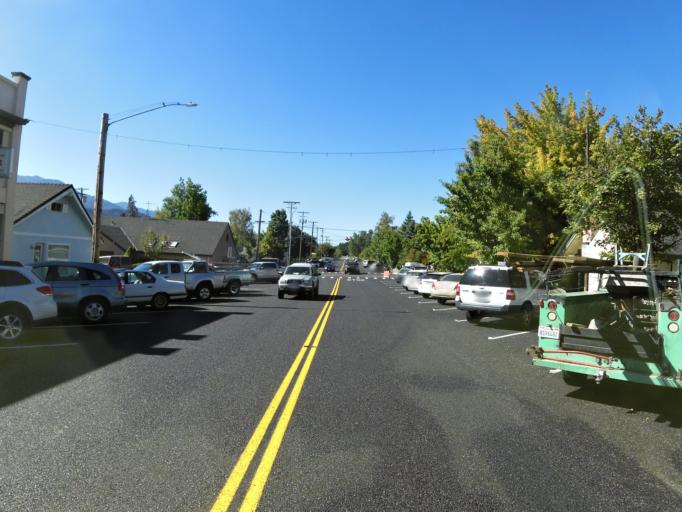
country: US
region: California
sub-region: Siskiyou County
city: Mount Shasta
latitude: 41.3153
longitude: -122.3134
